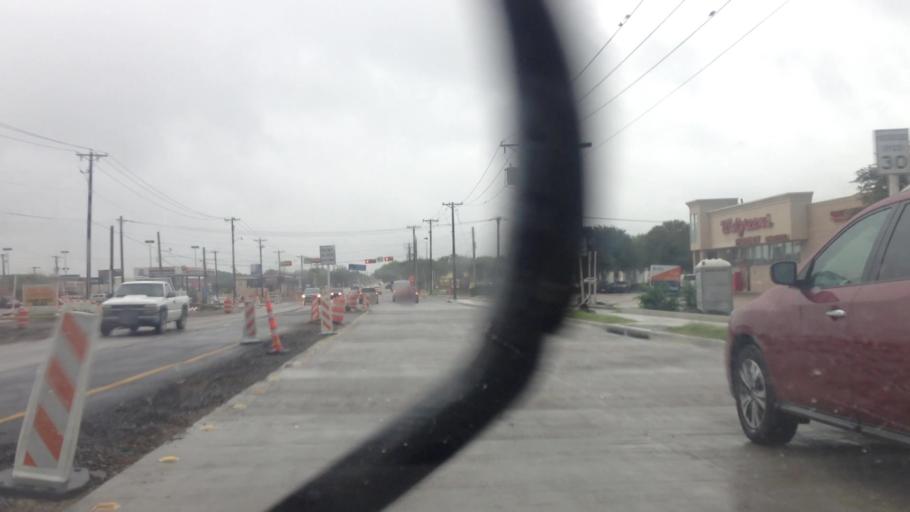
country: US
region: Texas
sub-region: Tarrant County
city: Watauga
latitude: 32.8738
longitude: -97.2378
